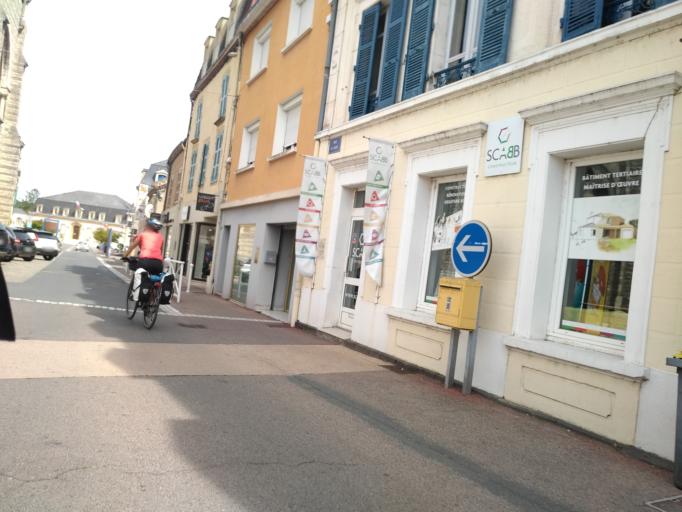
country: FR
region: Bourgogne
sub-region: Departement de Saone-et-Loire
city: Digoin
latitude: 46.4806
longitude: 3.9781
